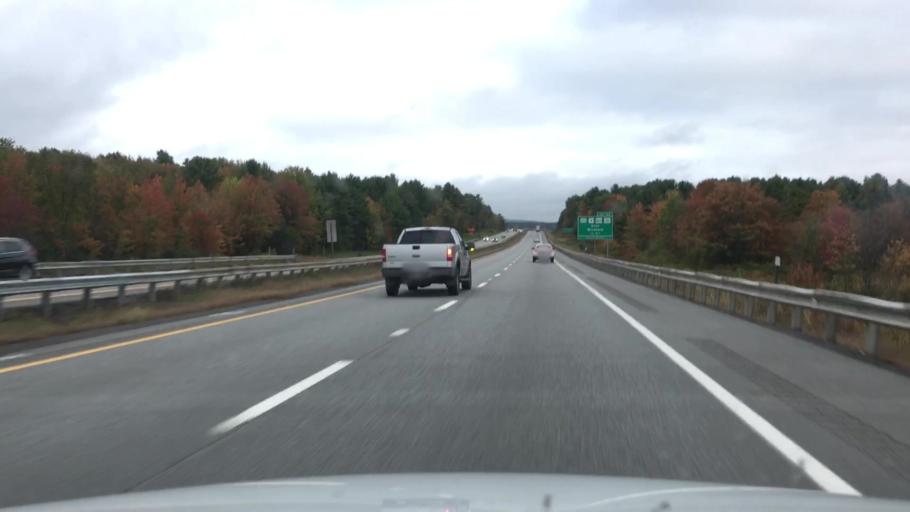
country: US
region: Maine
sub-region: Cumberland County
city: Cumberland Center
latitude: 43.8688
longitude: -70.3272
